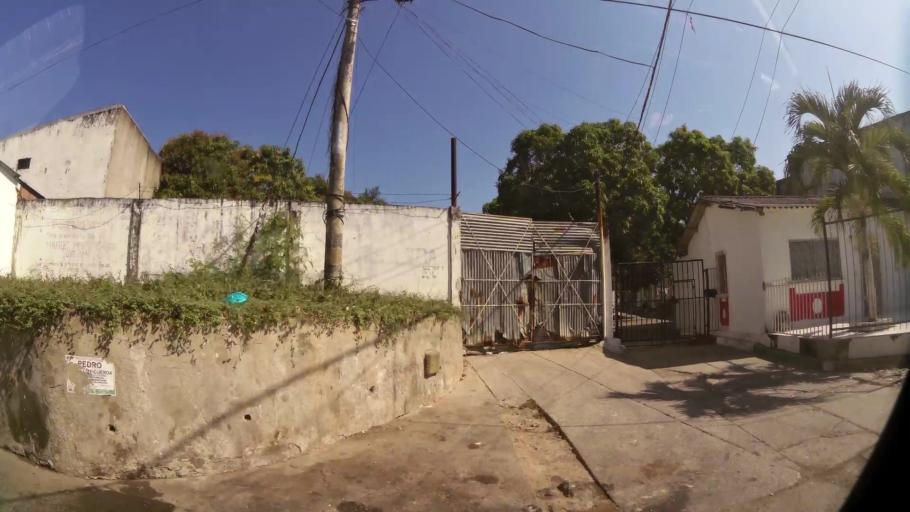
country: CO
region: Bolivar
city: Cartagena
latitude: 10.3845
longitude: -75.4636
